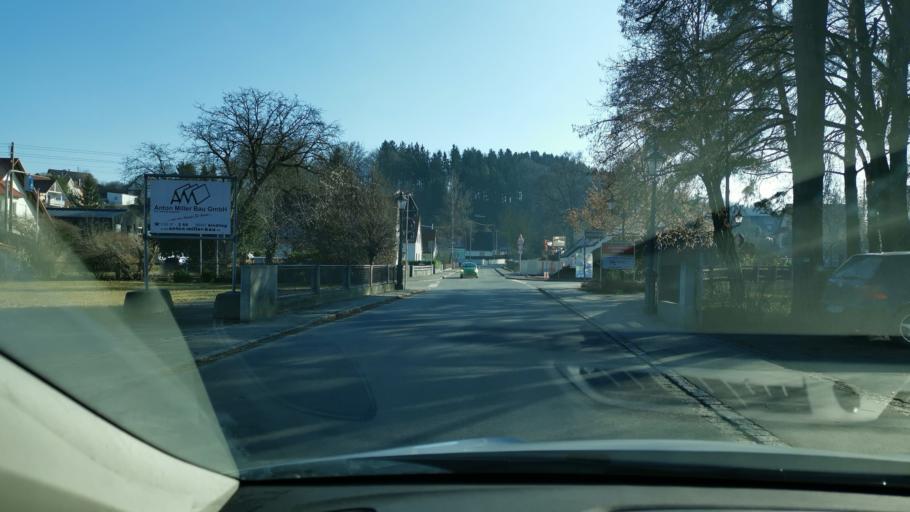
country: DE
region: Bavaria
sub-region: Swabia
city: Aindling
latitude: 48.5099
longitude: 10.9533
